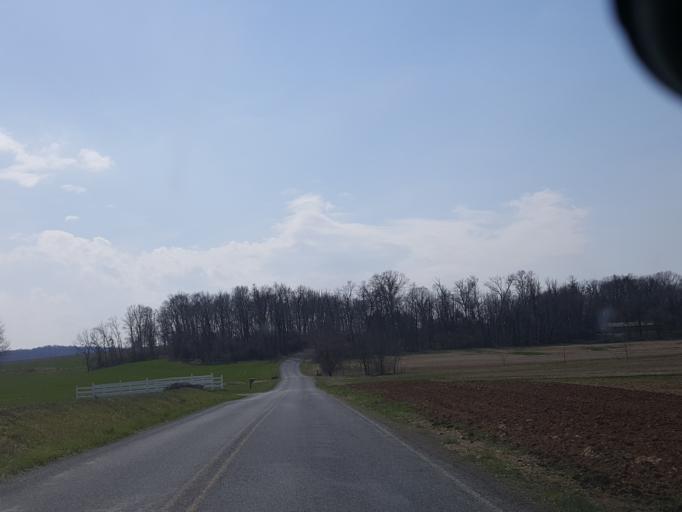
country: US
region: Pennsylvania
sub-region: Lebanon County
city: Campbelltown
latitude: 40.2889
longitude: -76.5477
